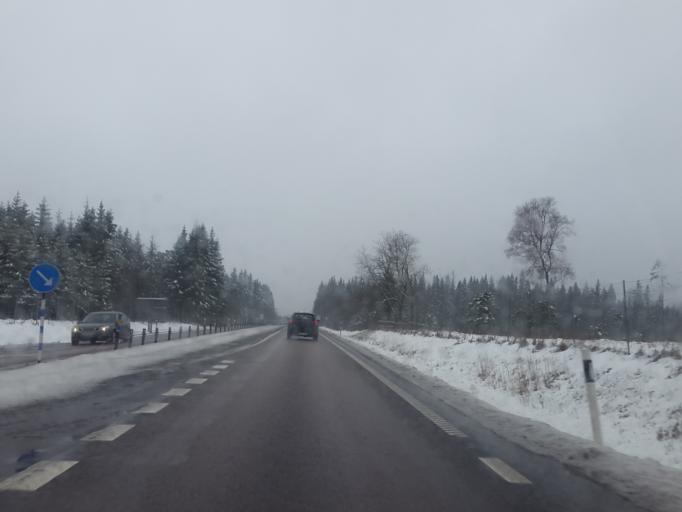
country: SE
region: Vaestra Goetaland
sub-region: Ulricehamns Kommun
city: Ulricehamn
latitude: 57.7962
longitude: 13.5671
